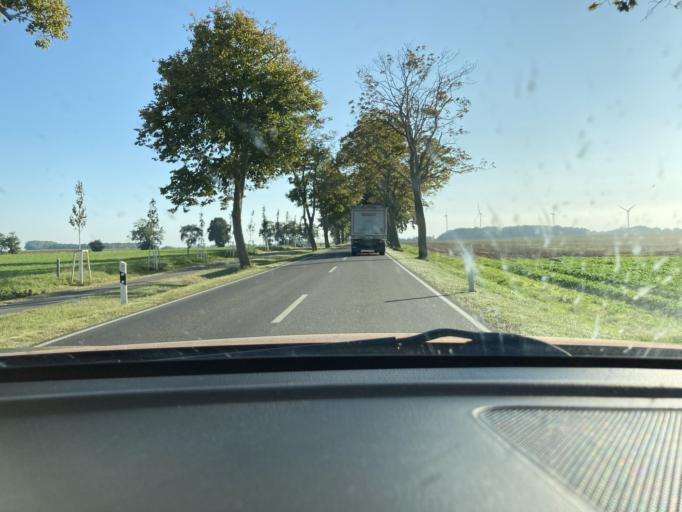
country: DE
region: Mecklenburg-Vorpommern
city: Anklam
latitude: 53.7935
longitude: 13.6660
